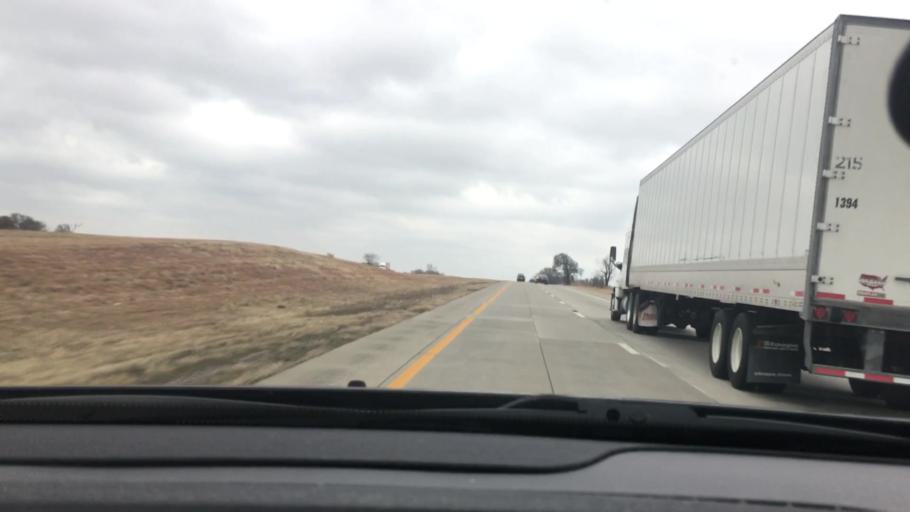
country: US
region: Oklahoma
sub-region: Atoka County
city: Atoka
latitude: 34.2198
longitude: -96.2286
